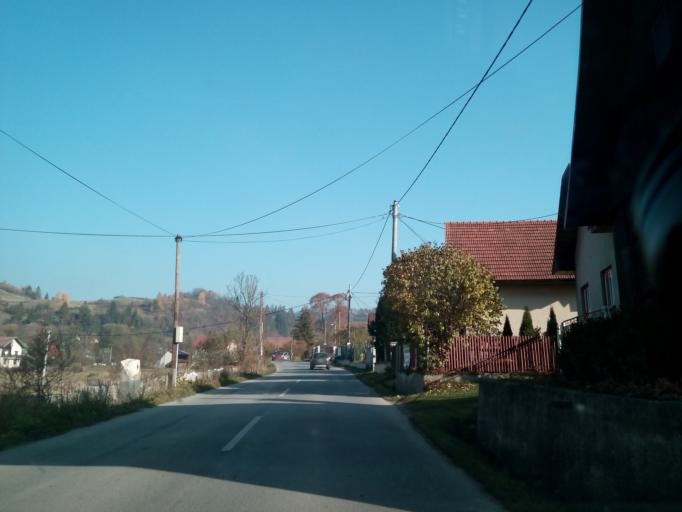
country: PL
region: Silesian Voivodeship
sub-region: Powiat cieszynski
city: Jaworzynka
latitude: 49.4417
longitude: 18.8909
